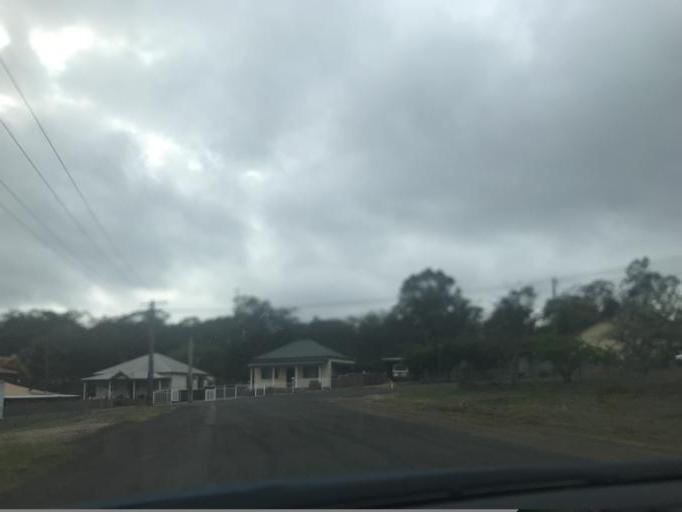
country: AU
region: New South Wales
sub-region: Cessnock
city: Cessnock
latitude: -32.9032
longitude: 151.2886
